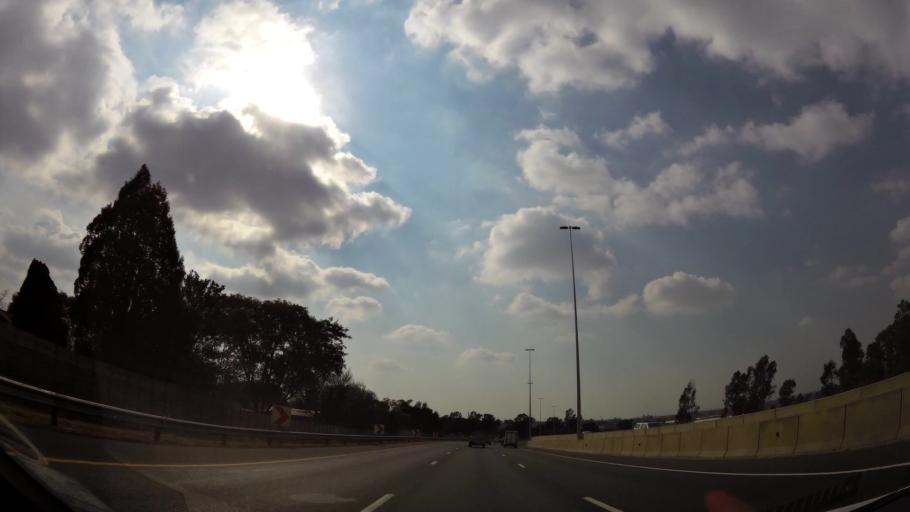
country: ZA
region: Gauteng
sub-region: Ekurhuleni Metropolitan Municipality
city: Benoni
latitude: -26.1647
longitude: 28.3577
